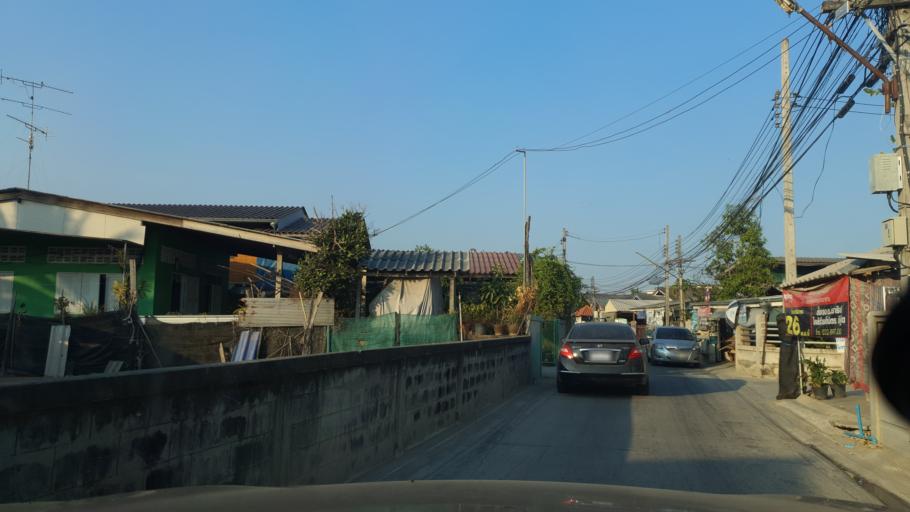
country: TH
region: Phetchaburi
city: Cha-am
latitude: 12.7944
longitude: 99.9638
